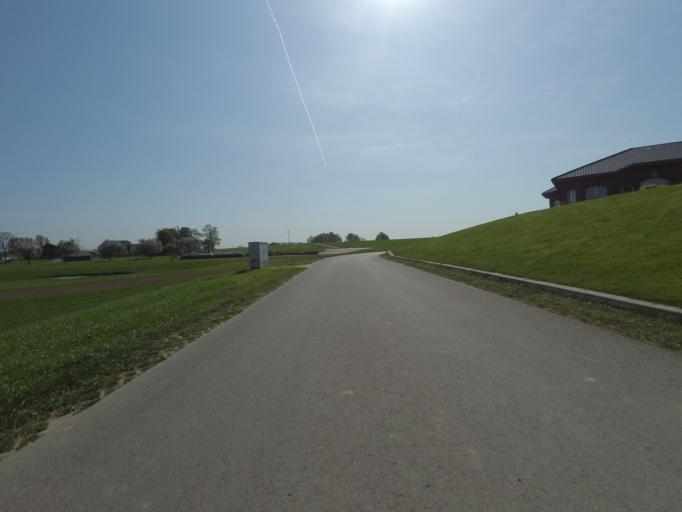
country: DE
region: North Rhine-Westphalia
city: Rees
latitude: 51.7185
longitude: 6.4386
